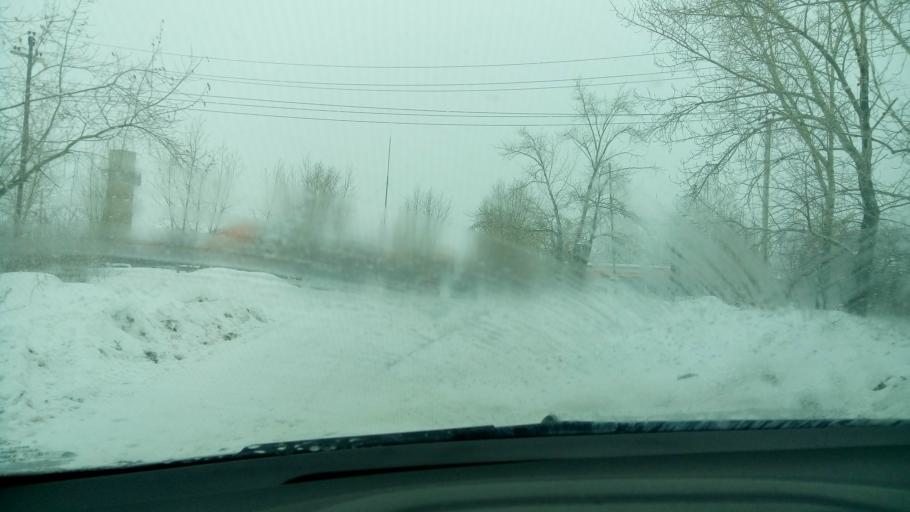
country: RU
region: Sverdlovsk
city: Bogdanovich
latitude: 56.8005
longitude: 62.0494
